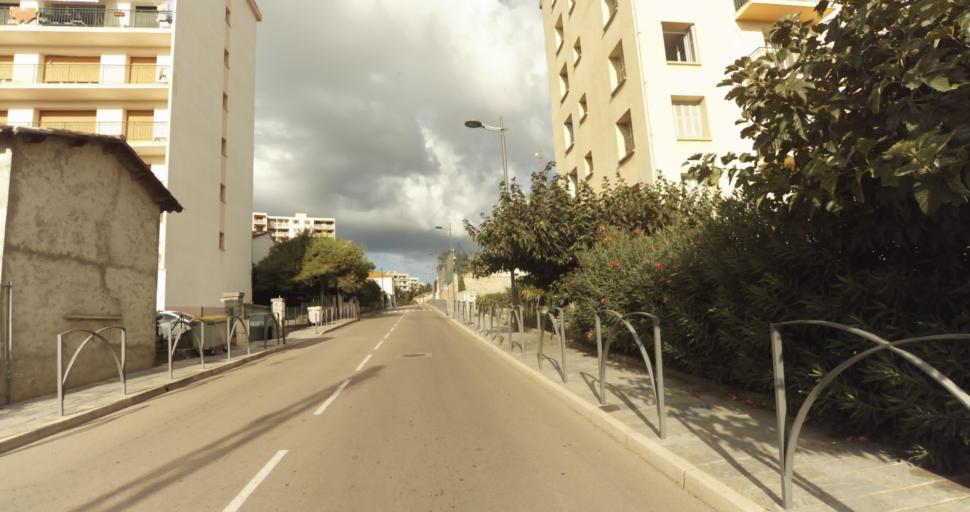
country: FR
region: Corsica
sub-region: Departement de la Corse-du-Sud
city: Ajaccio
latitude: 41.9292
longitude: 8.7318
